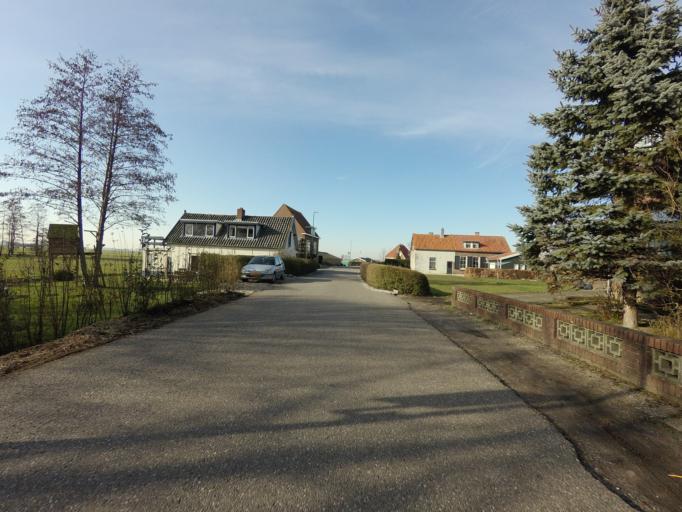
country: NL
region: South Holland
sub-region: Gemeente Giessenlanden
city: Giessenburg
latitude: 51.8490
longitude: 4.8778
